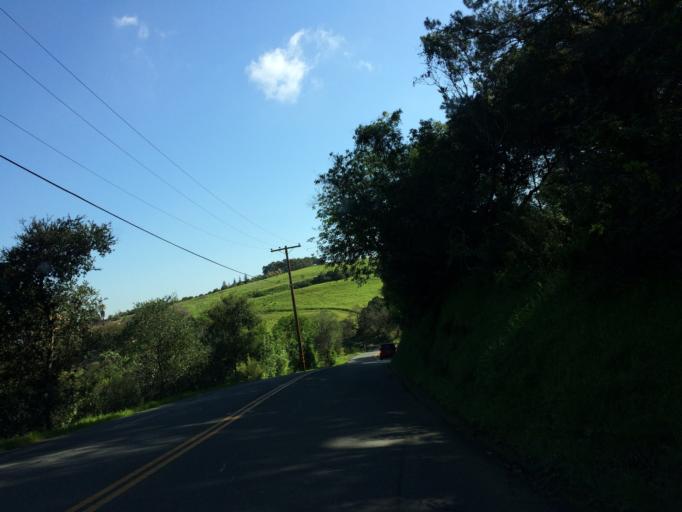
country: US
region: California
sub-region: Santa Clara County
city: Los Altos Hills
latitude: 37.3727
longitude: -122.1678
